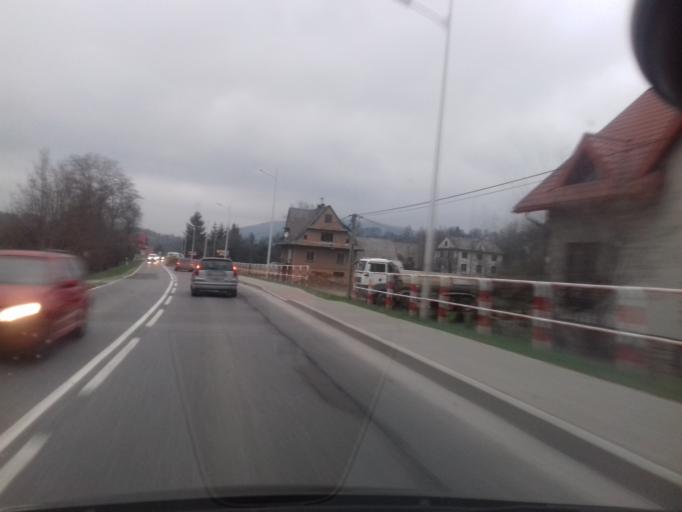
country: PL
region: Lesser Poland Voivodeship
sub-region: Powiat limanowski
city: Mszana Dolna
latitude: 49.6889
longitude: 20.0481
